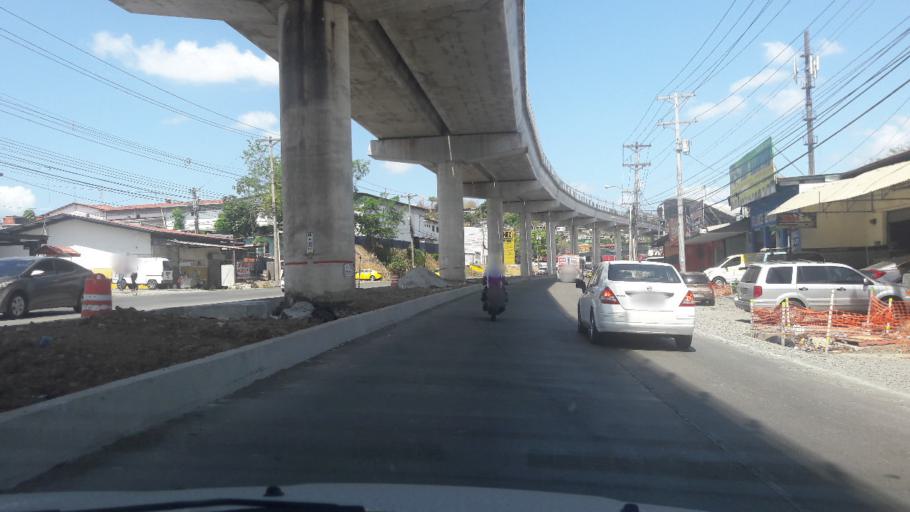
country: PA
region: Panama
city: San Miguelito
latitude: 9.0379
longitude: -79.5075
